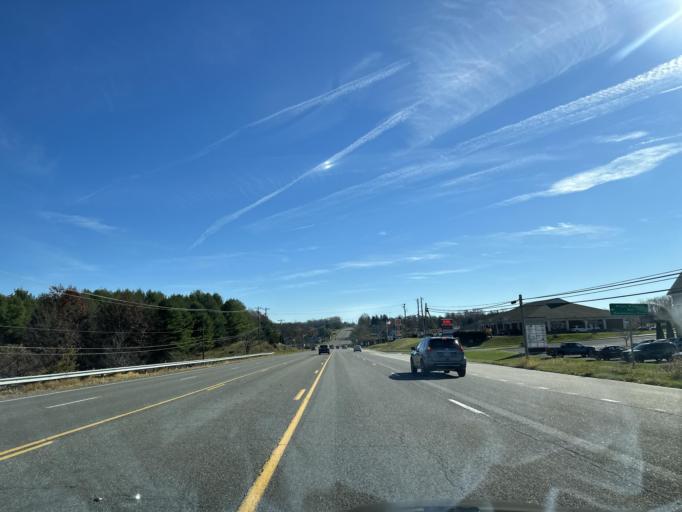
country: US
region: Virginia
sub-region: Augusta County
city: Fishersville
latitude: 38.1100
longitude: -78.9961
